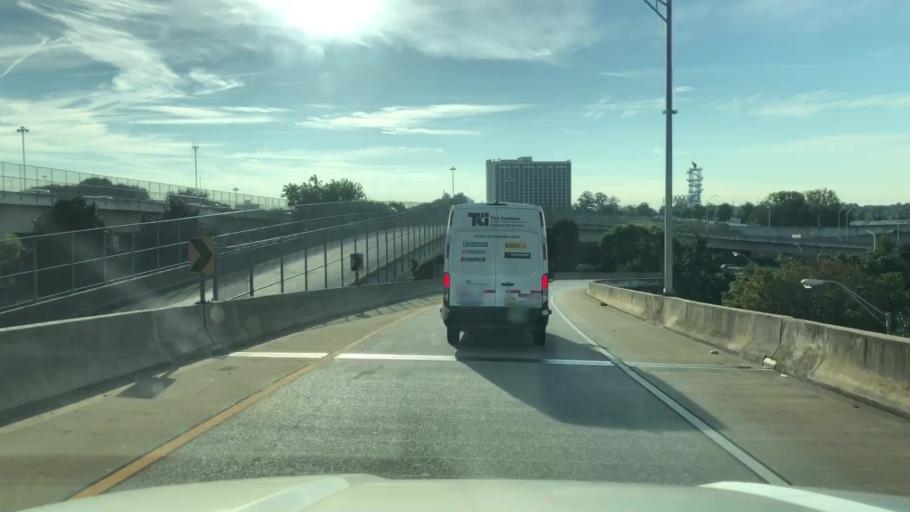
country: US
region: Georgia
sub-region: Fulton County
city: Atlanta
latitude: 33.7446
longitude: -84.3937
